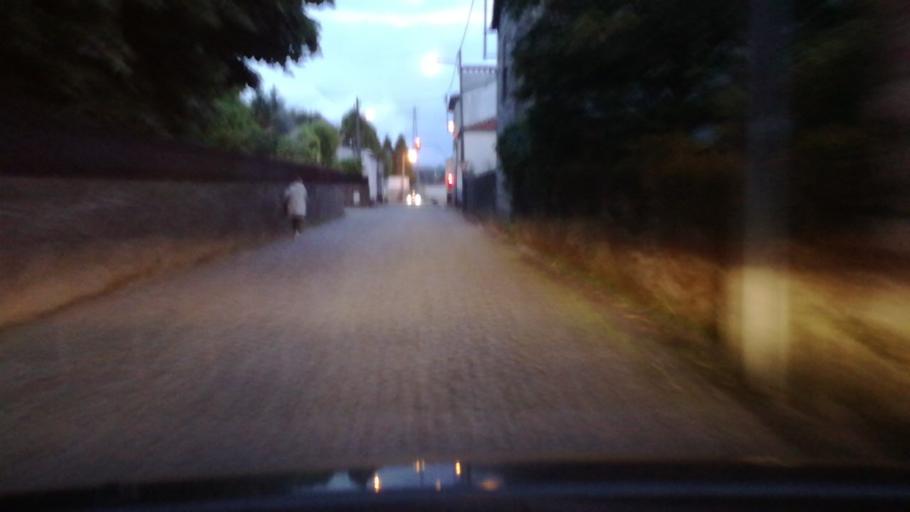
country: PT
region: Porto
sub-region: Maia
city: Anta
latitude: 41.2681
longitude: -8.6067
